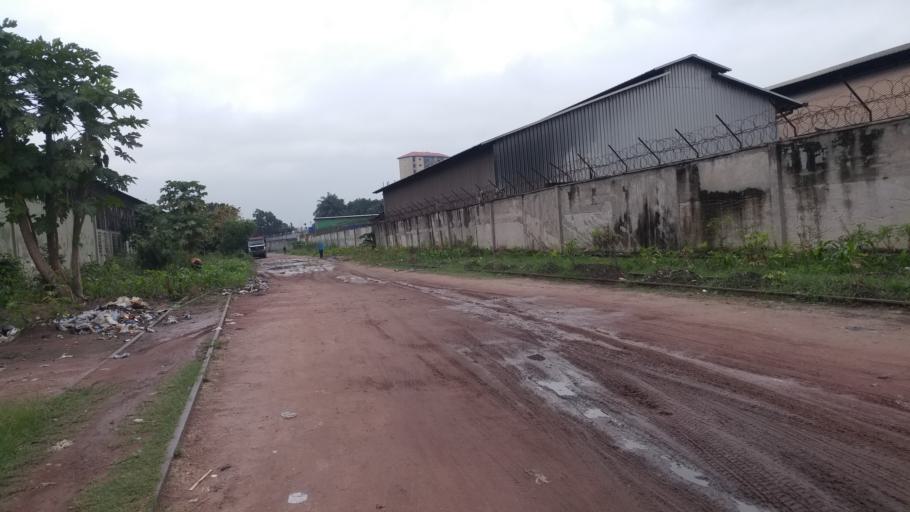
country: CD
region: Kinshasa
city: Kinshasa
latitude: -4.3226
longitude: 15.2740
